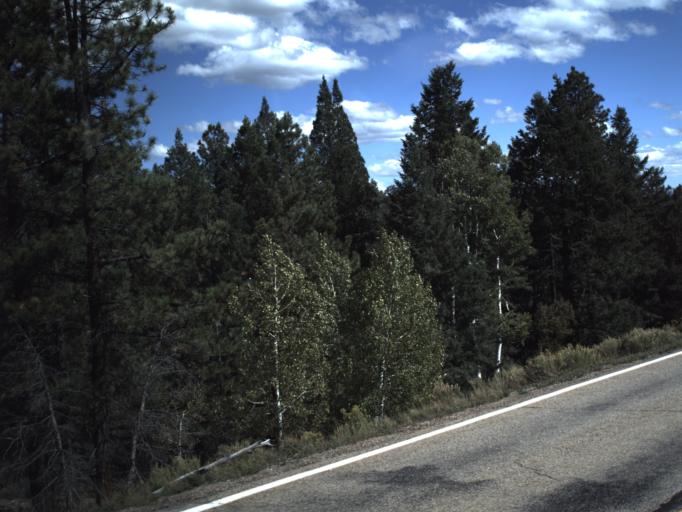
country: US
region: Utah
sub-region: Garfield County
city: Panguitch
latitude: 37.5110
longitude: -112.6318
